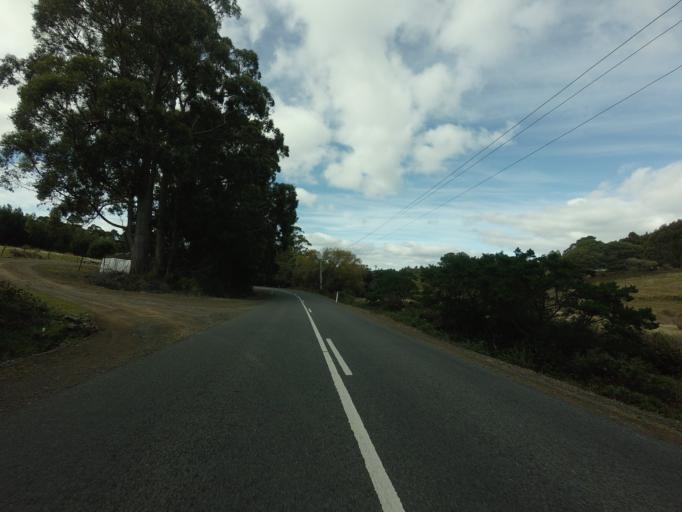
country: AU
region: Tasmania
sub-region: Clarence
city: Sandford
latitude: -43.1406
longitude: 147.8220
